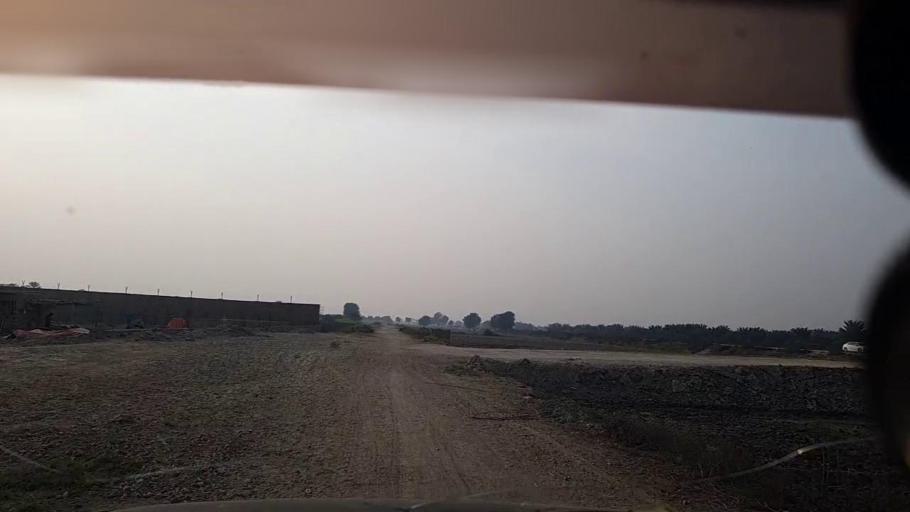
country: PK
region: Sindh
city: Gambat
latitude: 27.4355
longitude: 68.6057
